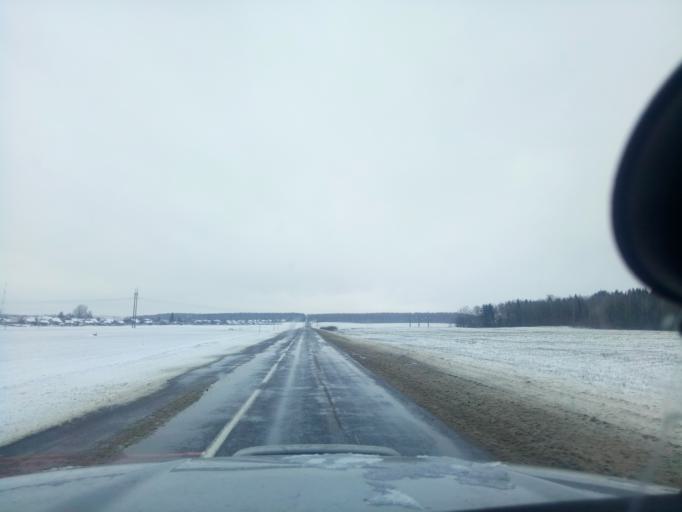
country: BY
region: Minsk
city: Kapyl'
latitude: 53.1159
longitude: 27.0647
